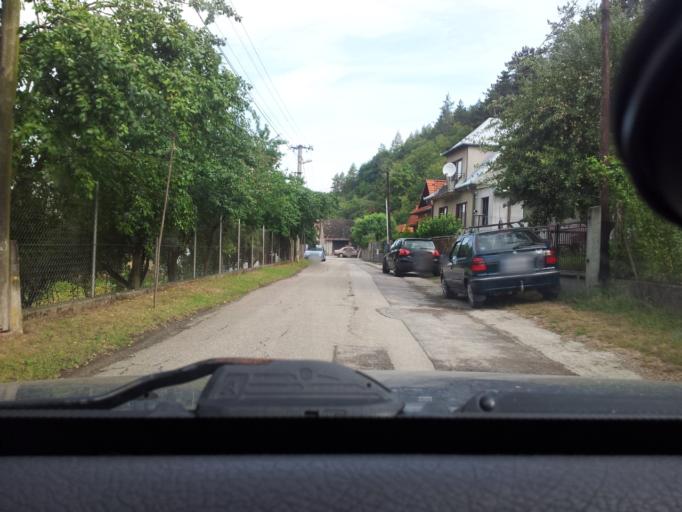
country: SK
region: Trenciansky
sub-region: Okres Trencin
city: Trencin
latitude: 48.8929
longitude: 18.0880
